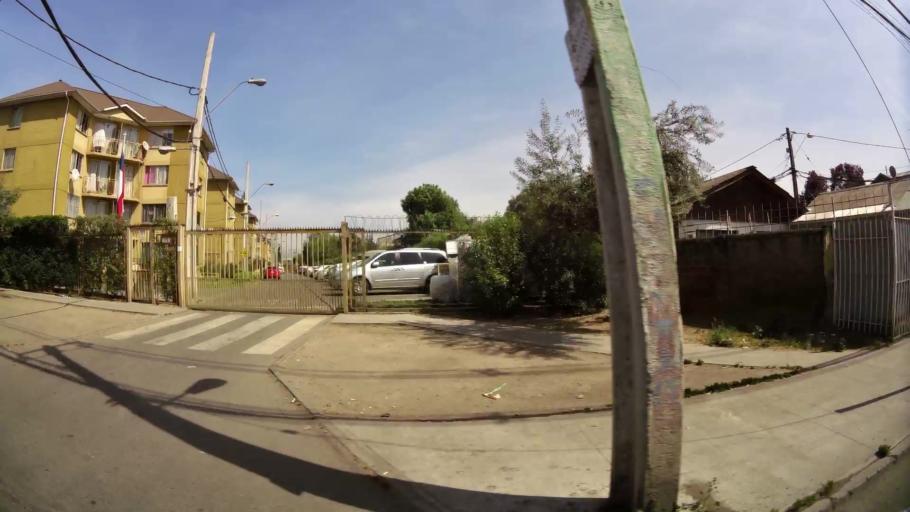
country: CL
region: Santiago Metropolitan
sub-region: Provincia de Santiago
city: Lo Prado
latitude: -33.4405
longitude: -70.7685
